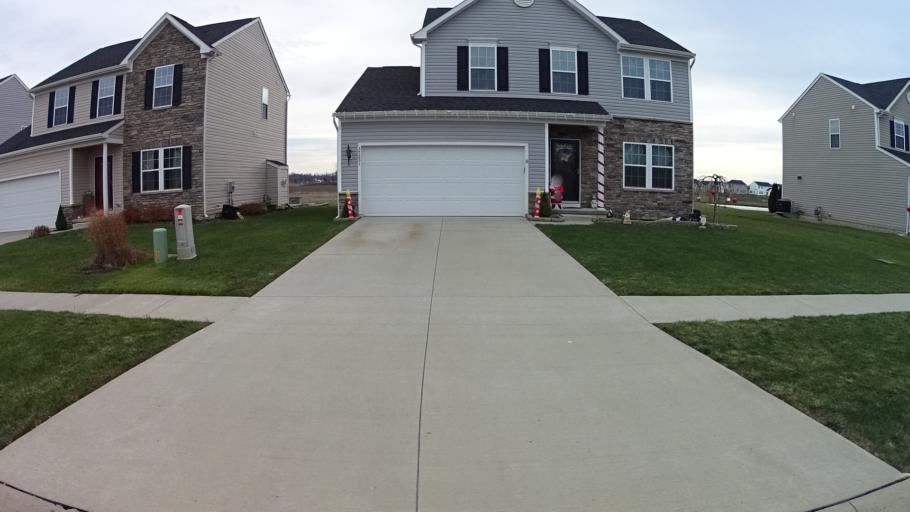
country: US
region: Ohio
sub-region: Lorain County
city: North Ridgeville
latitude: 41.3975
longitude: -82.0347
